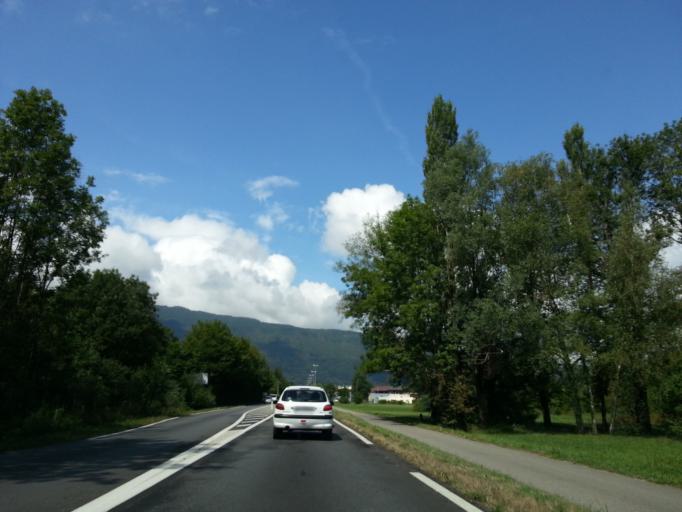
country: FR
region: Rhone-Alpes
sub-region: Departement de la Haute-Savoie
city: Saint-Jorioz
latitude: 45.8298
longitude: 6.1845
